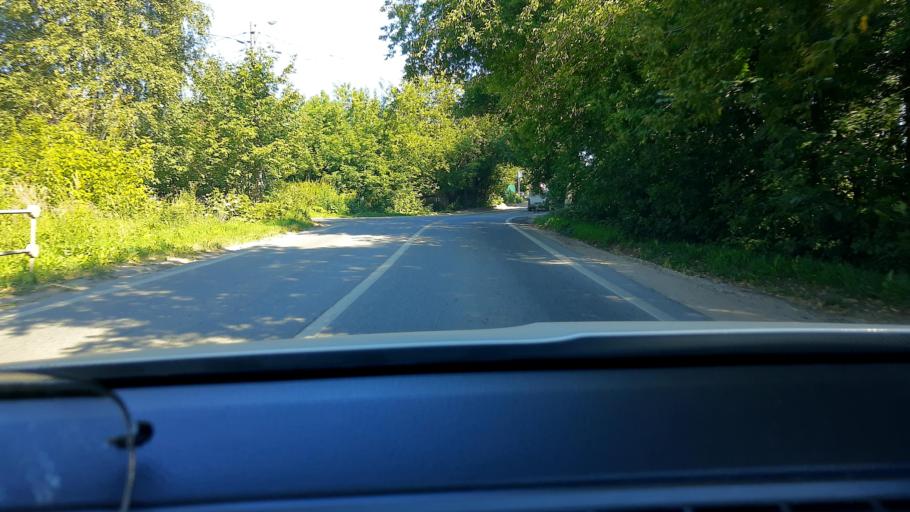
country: RU
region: Moskovskaya
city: Petrovo-Dal'neye
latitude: 55.7680
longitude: 37.2215
